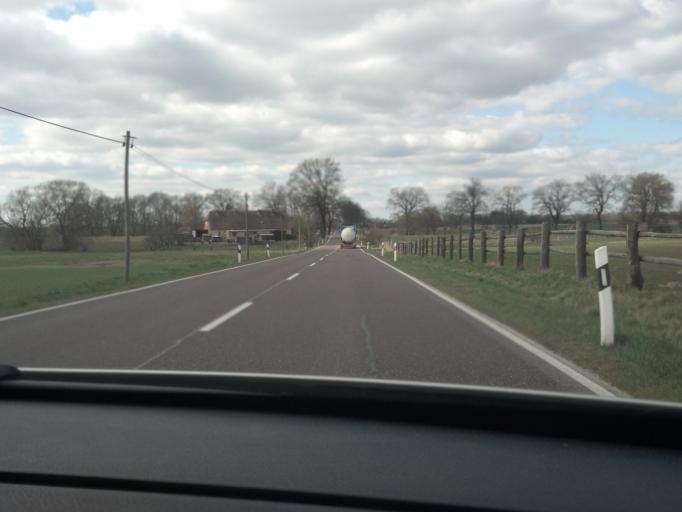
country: DE
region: Mecklenburg-Vorpommern
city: Robel
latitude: 53.3402
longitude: 12.5345
